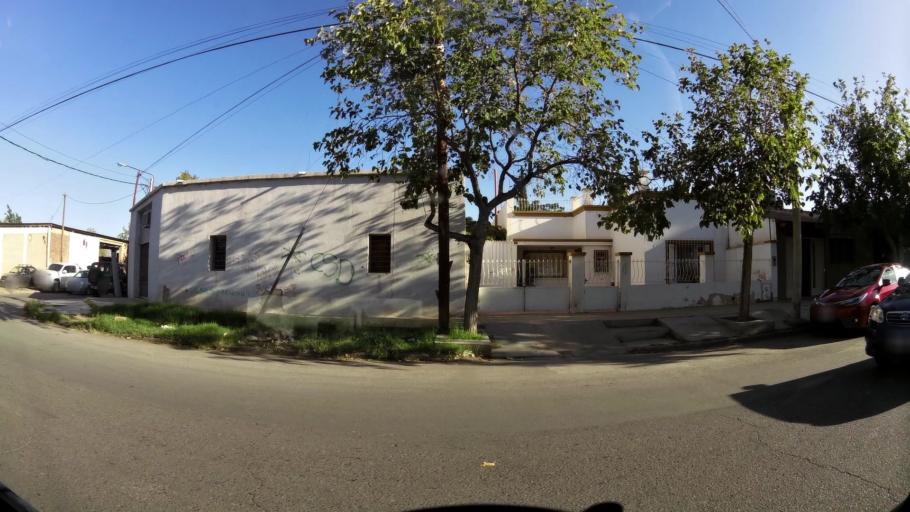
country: AR
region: San Juan
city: Villa Krause
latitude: -31.5522
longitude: -68.5162
